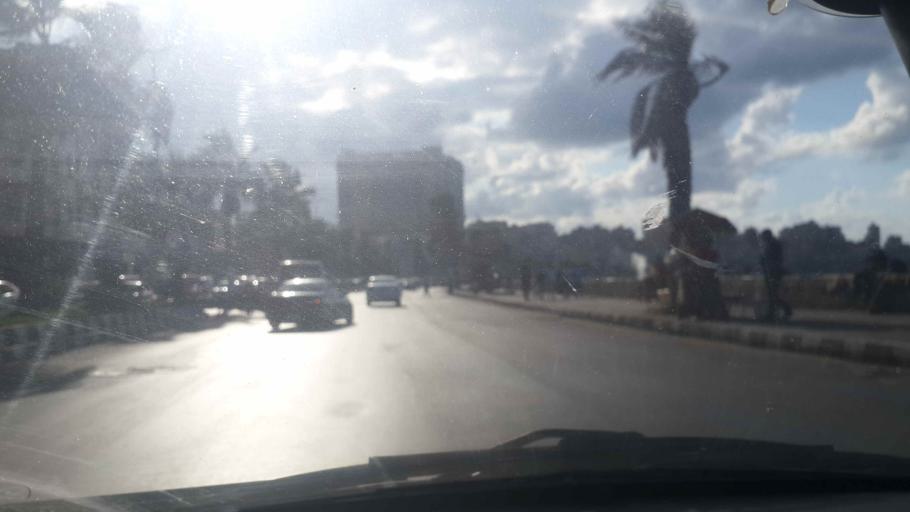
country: EG
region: Alexandria
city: Alexandria
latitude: 31.2005
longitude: 29.8959
